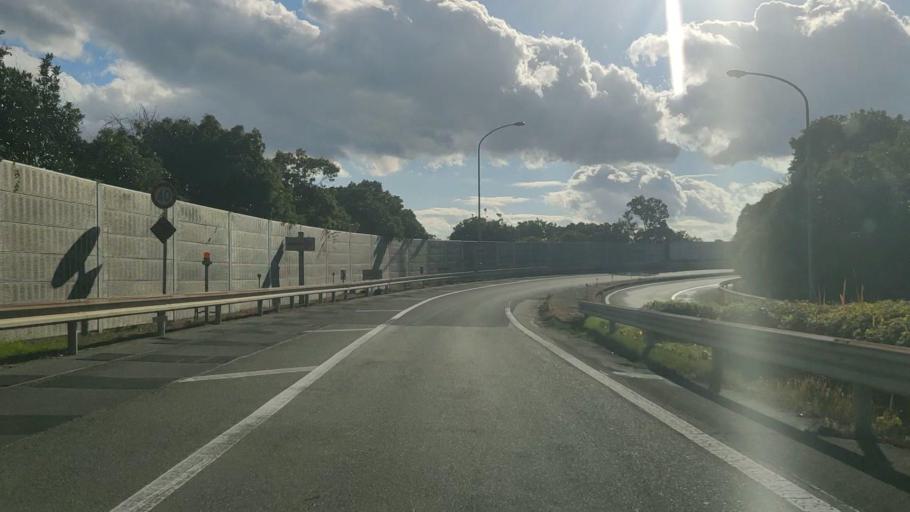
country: JP
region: Fukuoka
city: Nogata
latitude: 33.7800
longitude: 130.7424
